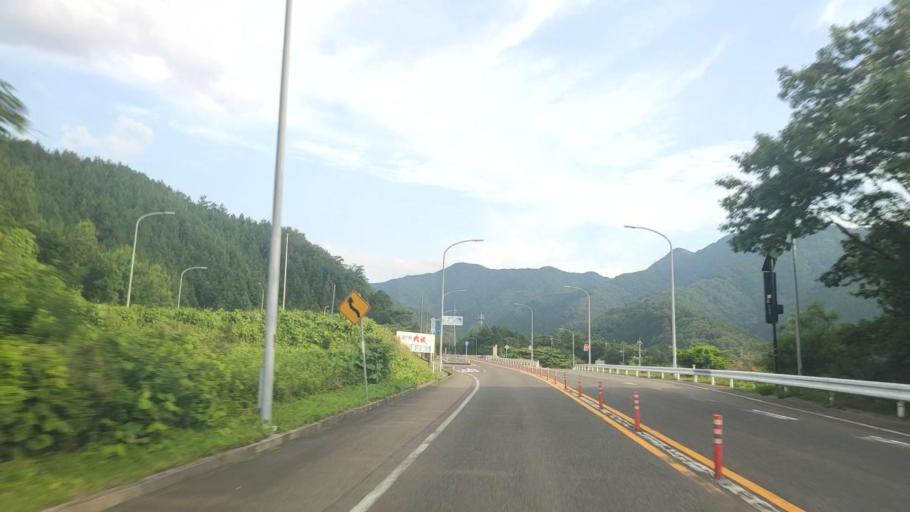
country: JP
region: Tottori
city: Kurayoshi
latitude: 35.3303
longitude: 133.7550
